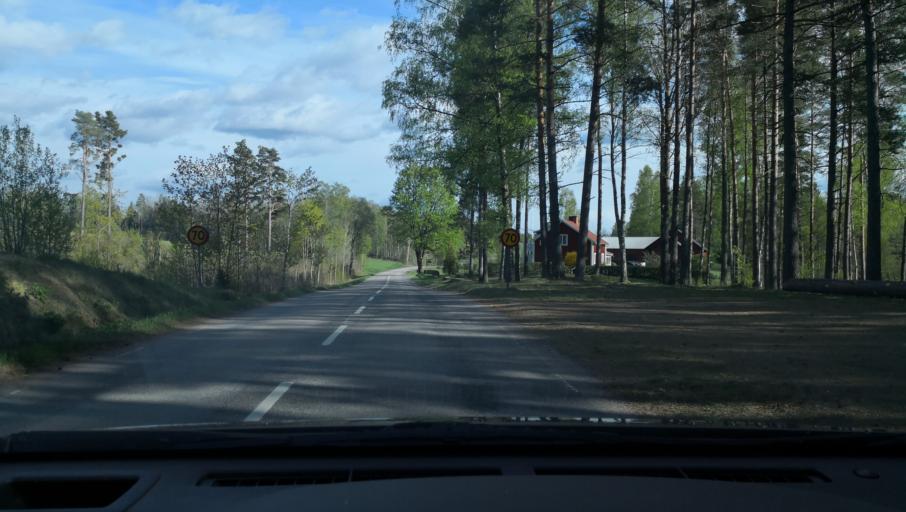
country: SE
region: OErebro
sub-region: Askersunds Kommun
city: Asbro
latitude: 58.9780
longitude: 15.0615
